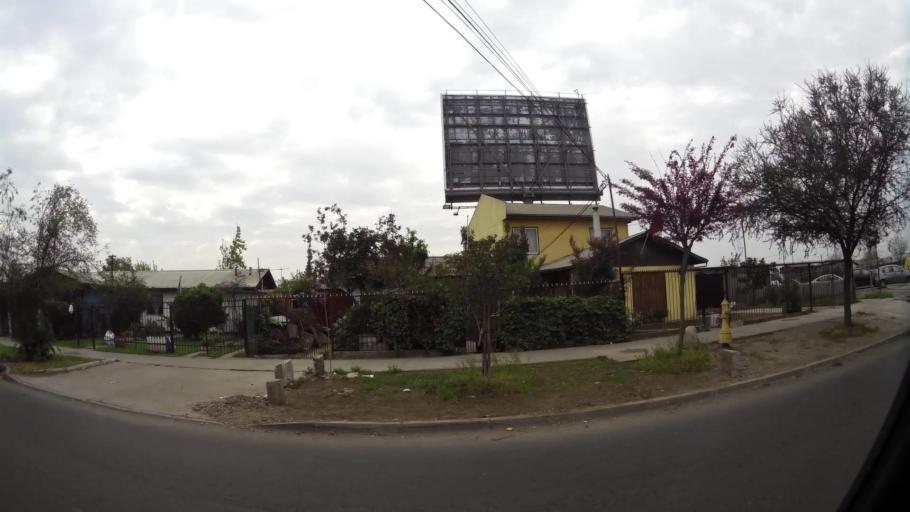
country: CL
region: Santiago Metropolitan
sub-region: Provincia de Santiago
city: Lo Prado
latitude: -33.4968
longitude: -70.7464
